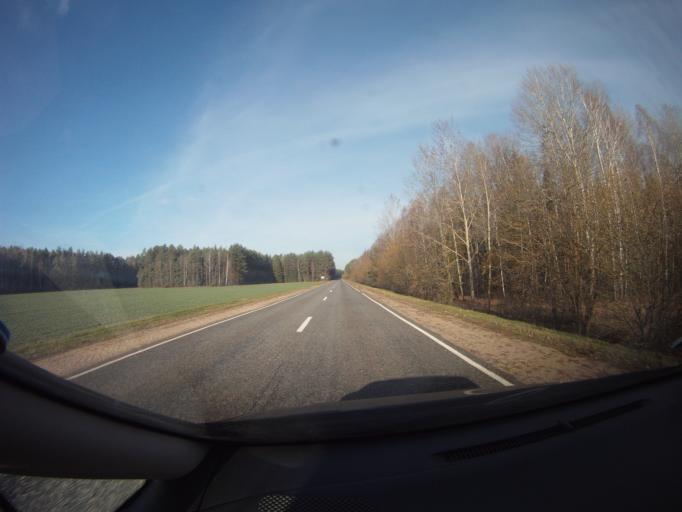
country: BY
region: Minsk
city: Il'ya
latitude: 54.5204
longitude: 27.2210
